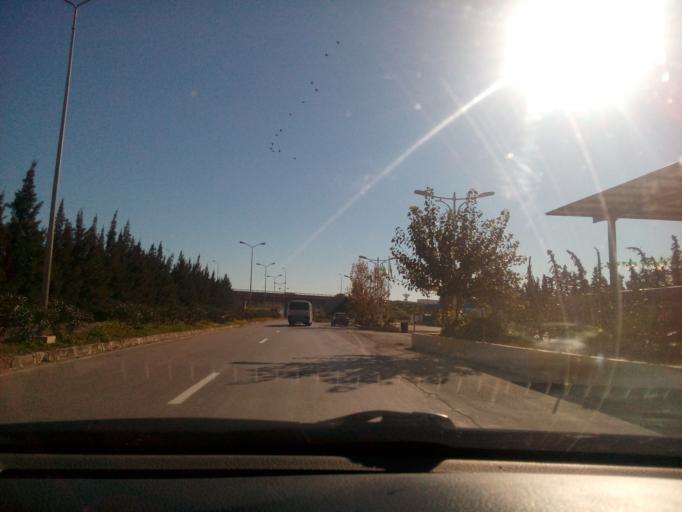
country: DZ
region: Relizane
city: Relizane
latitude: 35.7183
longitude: 0.5075
